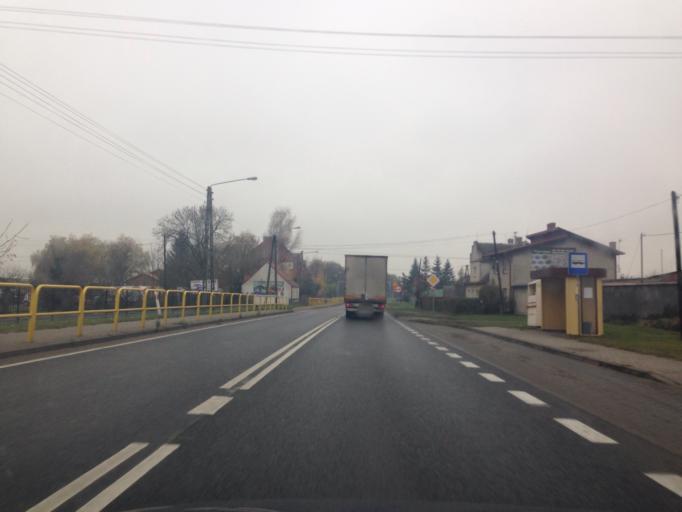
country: PL
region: Kujawsko-Pomorskie
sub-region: Powiat nakielski
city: Naklo nad Notecia
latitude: 53.1590
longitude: 17.6350
